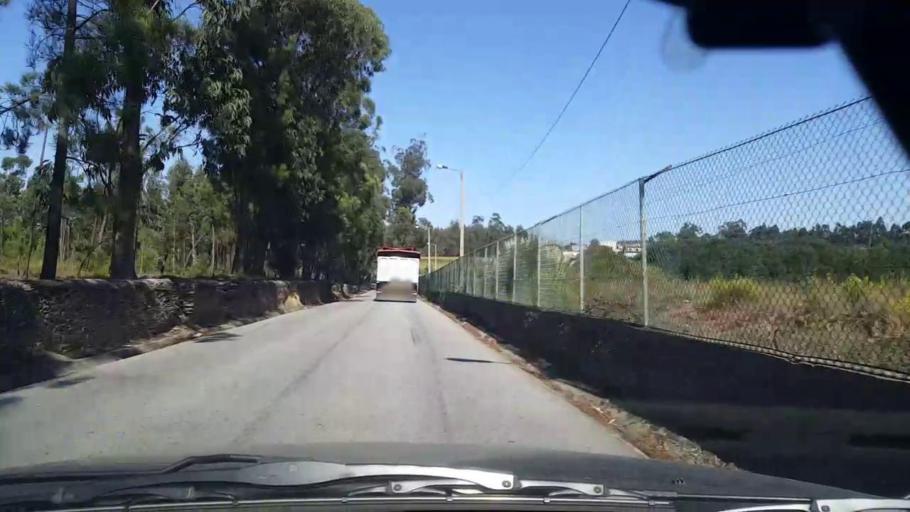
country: PT
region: Braga
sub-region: Vila Nova de Famalicao
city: Ribeirao
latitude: 41.3687
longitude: -8.6160
